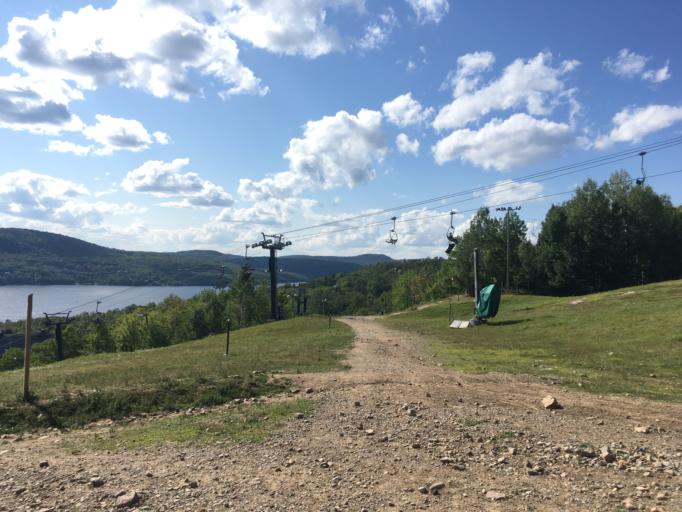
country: CA
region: Quebec
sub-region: Laurentides
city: Mont-Tremblant
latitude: 46.2151
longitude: -74.5814
